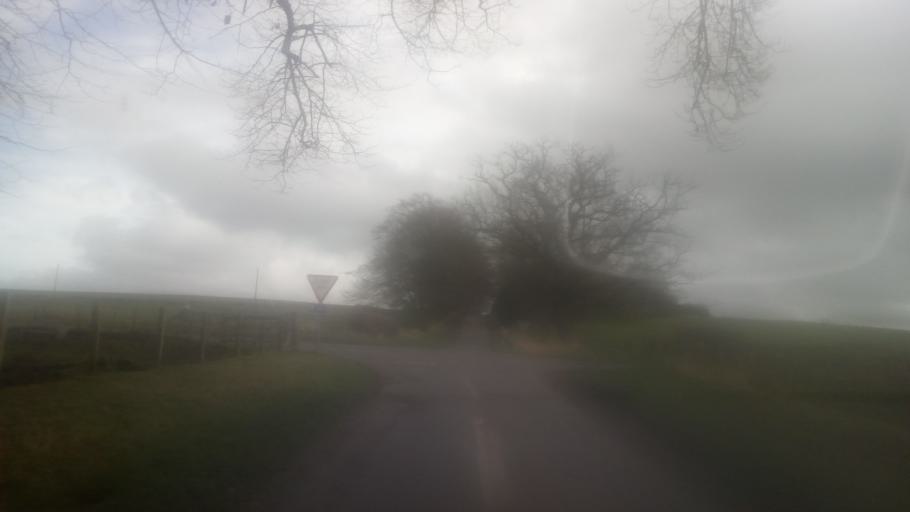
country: GB
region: Scotland
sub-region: The Scottish Borders
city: Jedburgh
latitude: 55.4897
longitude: -2.4793
